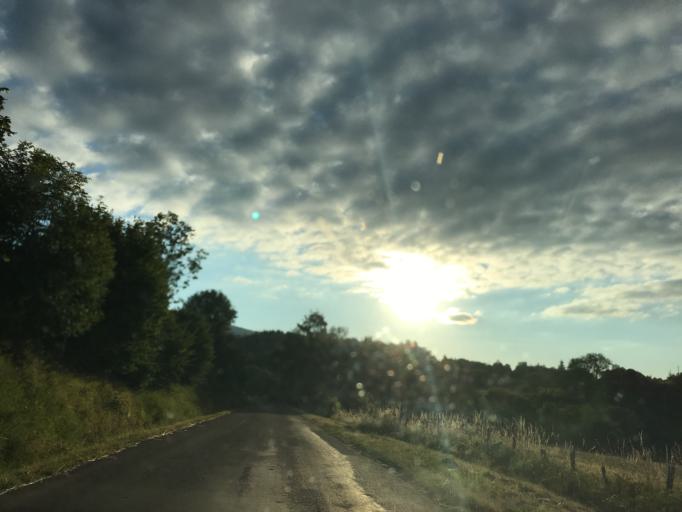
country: FR
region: Rhone-Alpes
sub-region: Departement de la Loire
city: Noiretable
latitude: 45.7736
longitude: 3.8153
